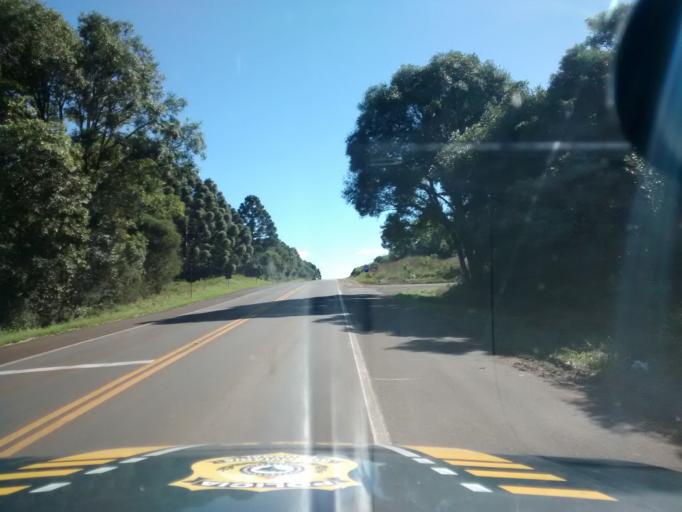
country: BR
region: Rio Grande do Sul
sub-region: Vacaria
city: Vacaria
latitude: -28.3563
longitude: -51.1088
